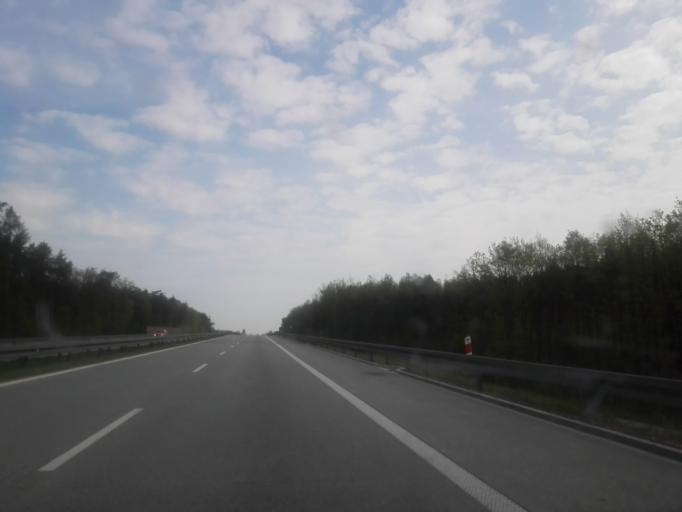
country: PL
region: Lodz Voivodeship
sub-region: Powiat rawski
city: Rawa Mazowiecka
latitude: 51.7278
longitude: 20.2273
